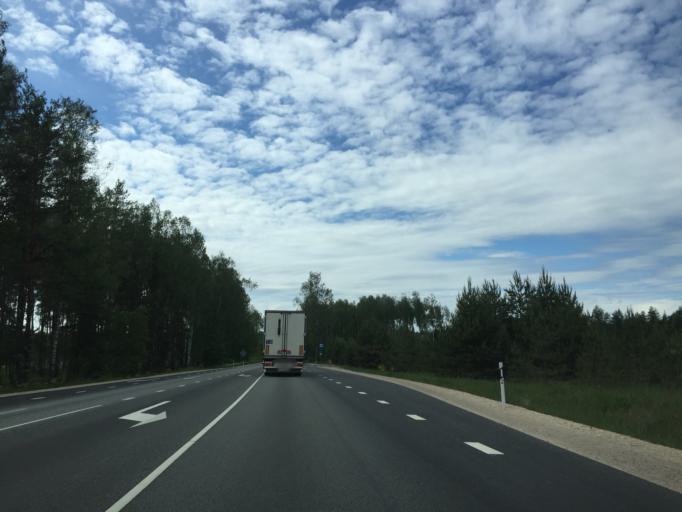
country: LV
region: Ikskile
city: Ikskile
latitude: 56.8855
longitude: 24.4952
